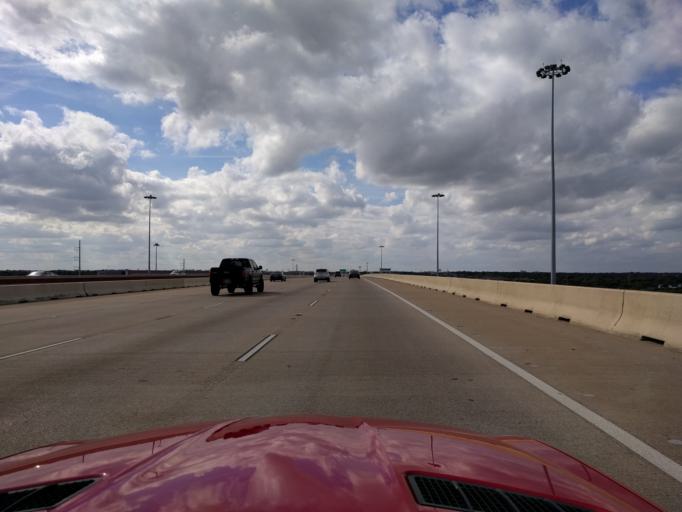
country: US
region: Texas
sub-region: Collin County
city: Plano
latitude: 33.0042
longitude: -96.7068
